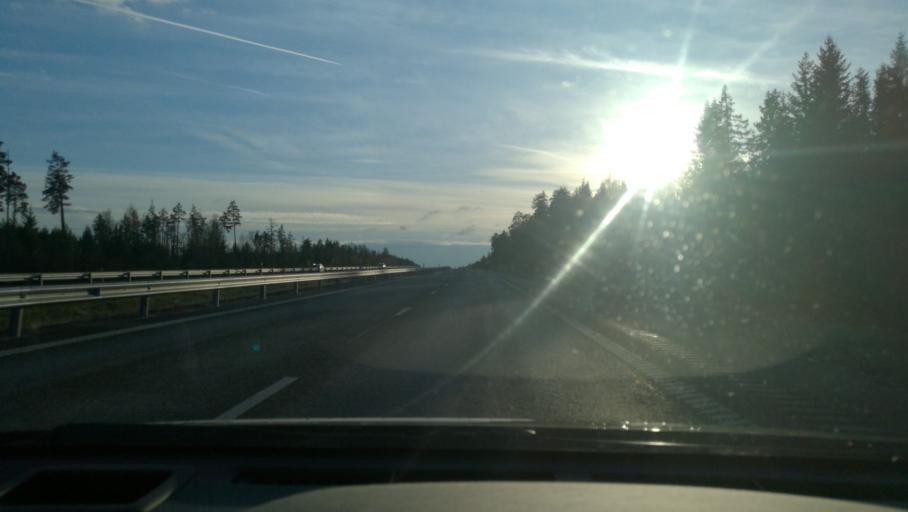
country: SE
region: Vaestmanland
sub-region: Kopings Kommun
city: Koping
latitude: 59.4845
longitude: 15.9121
